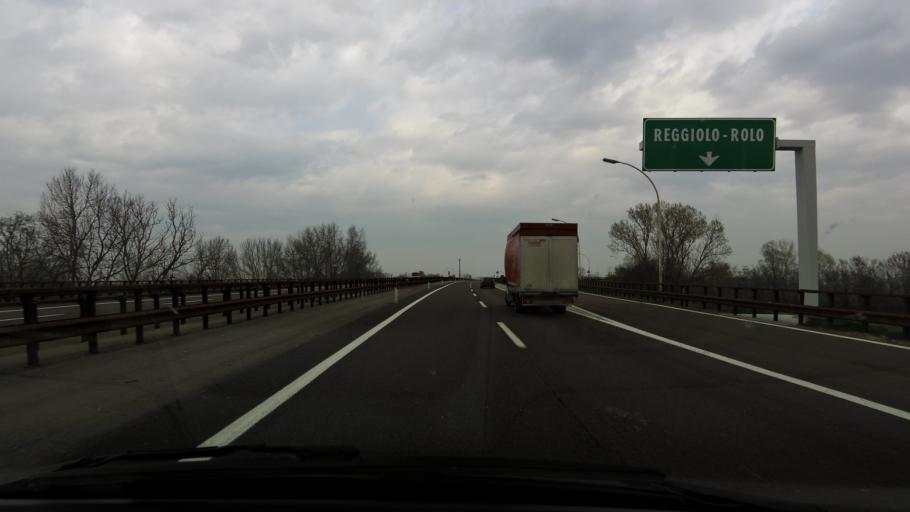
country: IT
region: Emilia-Romagna
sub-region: Provincia di Reggio Emilia
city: Rolo
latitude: 44.9081
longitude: 10.8484
